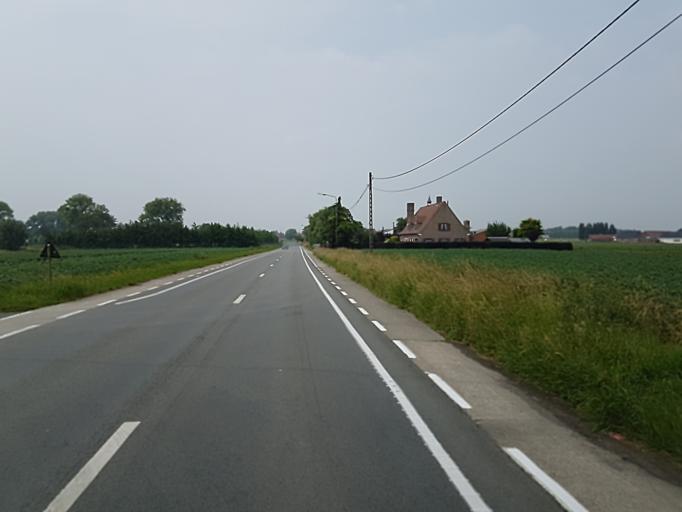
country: BE
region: Flanders
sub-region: Provincie West-Vlaanderen
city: Ingelmunster
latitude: 50.9455
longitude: 3.2344
